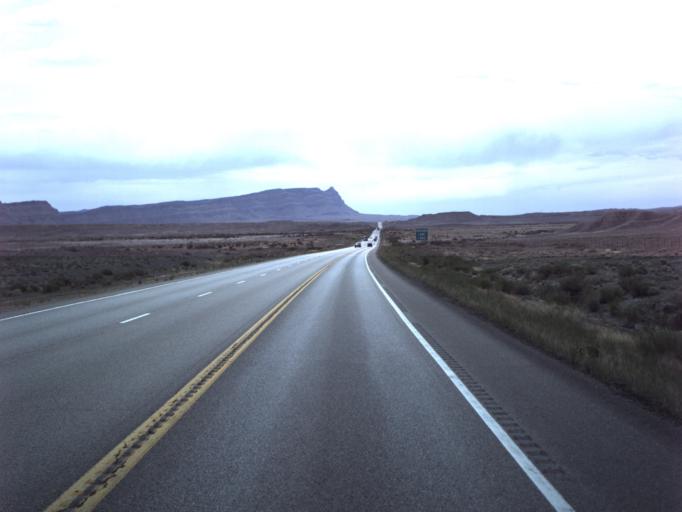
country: US
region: Utah
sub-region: Carbon County
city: East Carbon City
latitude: 39.3388
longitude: -110.3718
